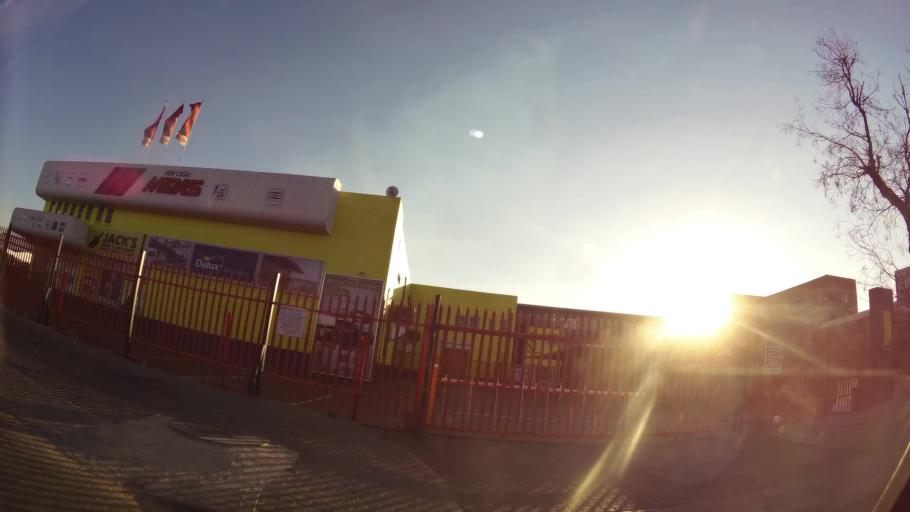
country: ZA
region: Gauteng
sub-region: Ekurhuleni Metropolitan Municipality
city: Germiston
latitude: -26.2706
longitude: 28.1231
